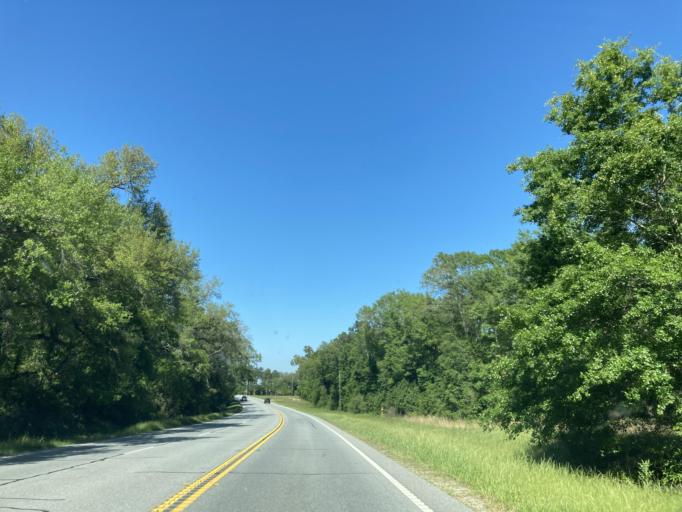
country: US
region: Georgia
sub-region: Baker County
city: Newton
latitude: 31.2935
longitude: -84.3506
